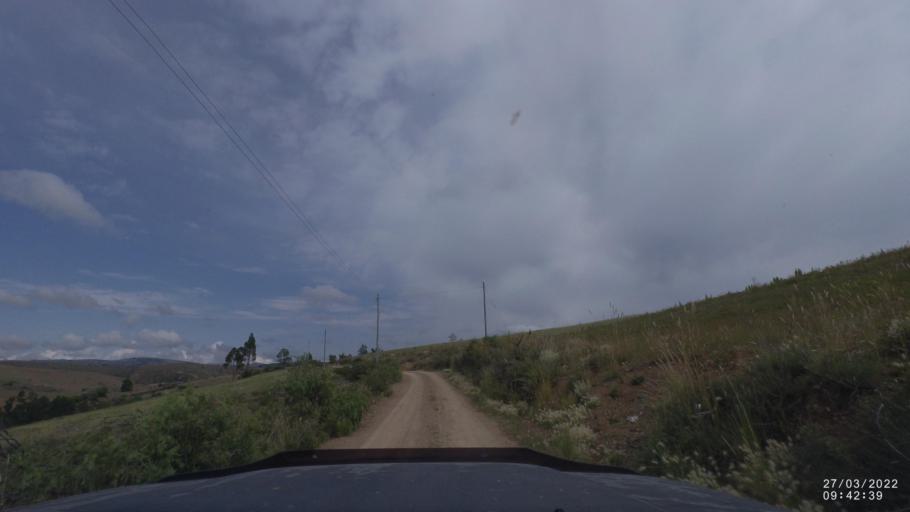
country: BO
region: Cochabamba
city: Cliza
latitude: -17.7517
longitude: -65.9036
